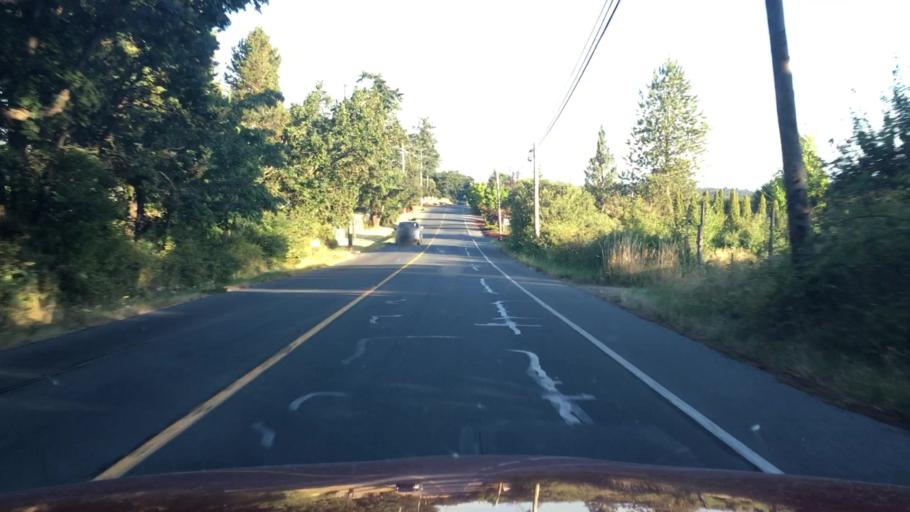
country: CA
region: British Columbia
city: Victoria
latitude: 48.4859
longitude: -123.3552
